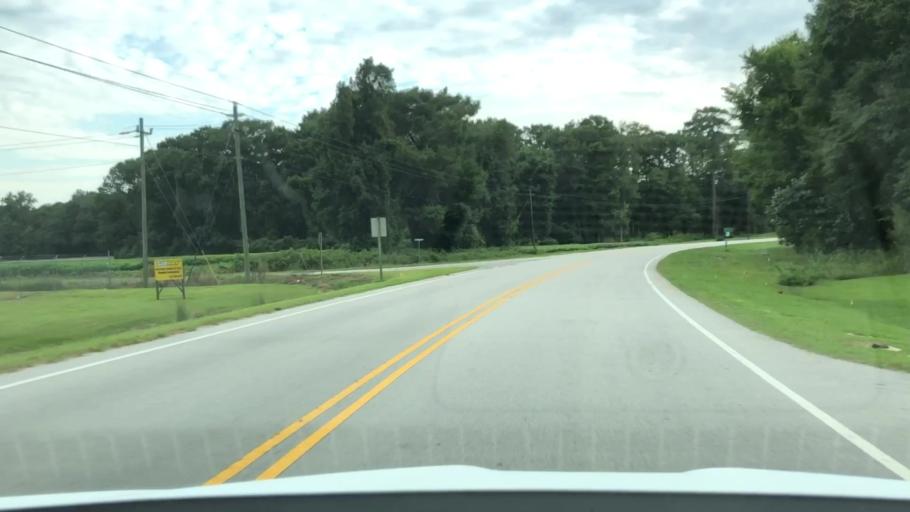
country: US
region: North Carolina
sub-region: Jones County
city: Trenton
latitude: 35.0567
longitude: -77.3572
